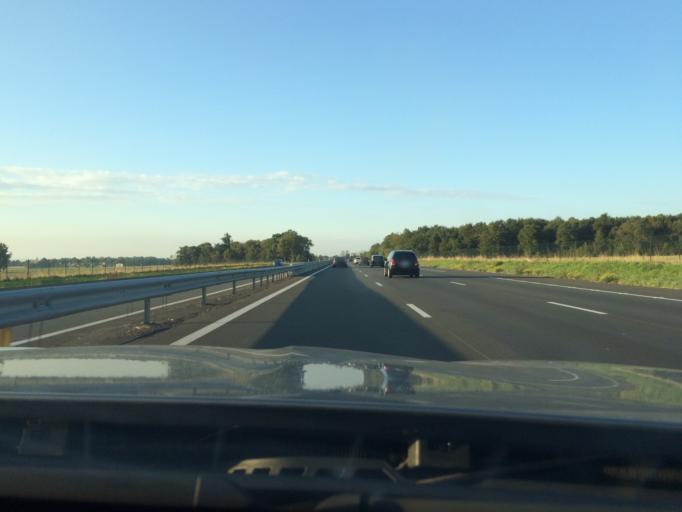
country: FR
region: Ile-de-France
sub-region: Departement de l'Essonne
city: Le Coudray-Montceaux
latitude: 48.5443
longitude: 2.4970
